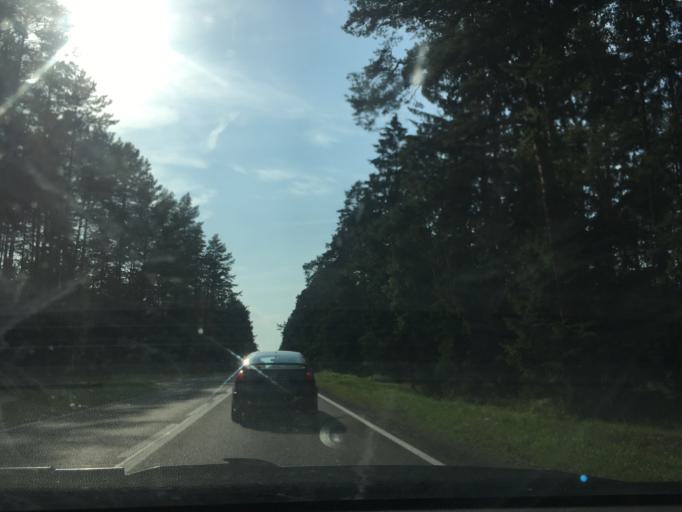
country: PL
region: Podlasie
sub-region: Powiat bialostocki
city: Suprasl
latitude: 53.1255
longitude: 23.3826
